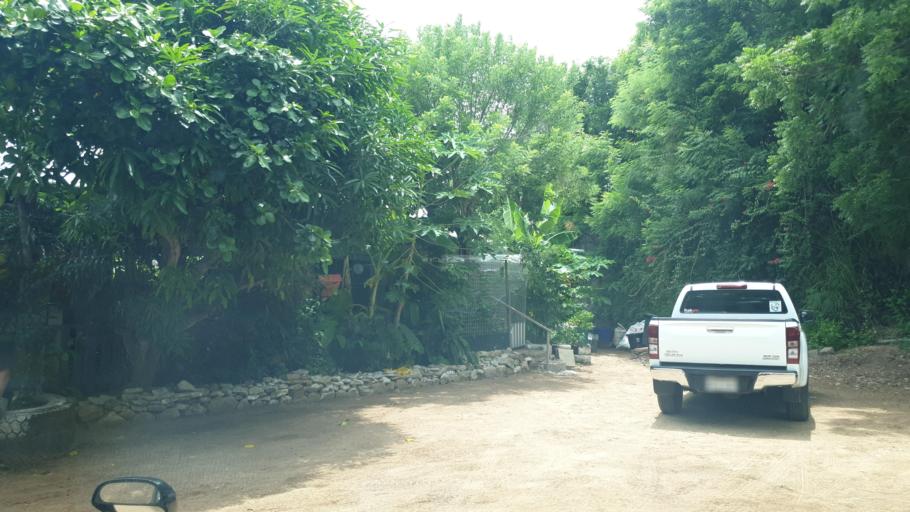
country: PG
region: National Capital
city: Port Moresby
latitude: -9.5284
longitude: 147.2499
